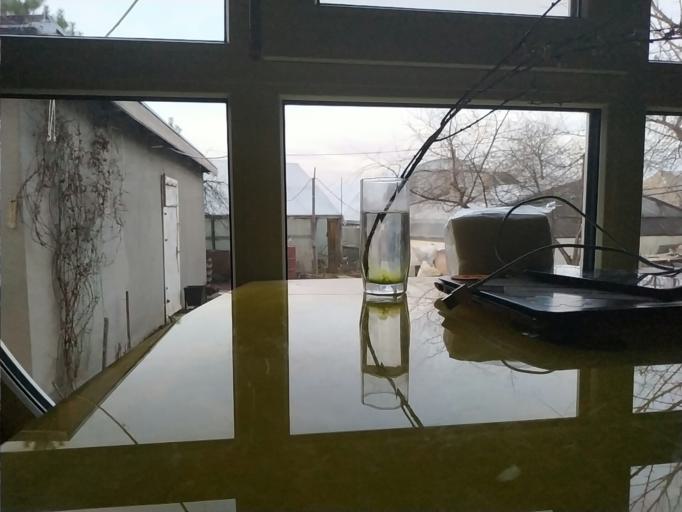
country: RU
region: Republic of Karelia
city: Suoyarvi
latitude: 62.4956
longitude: 31.9831
